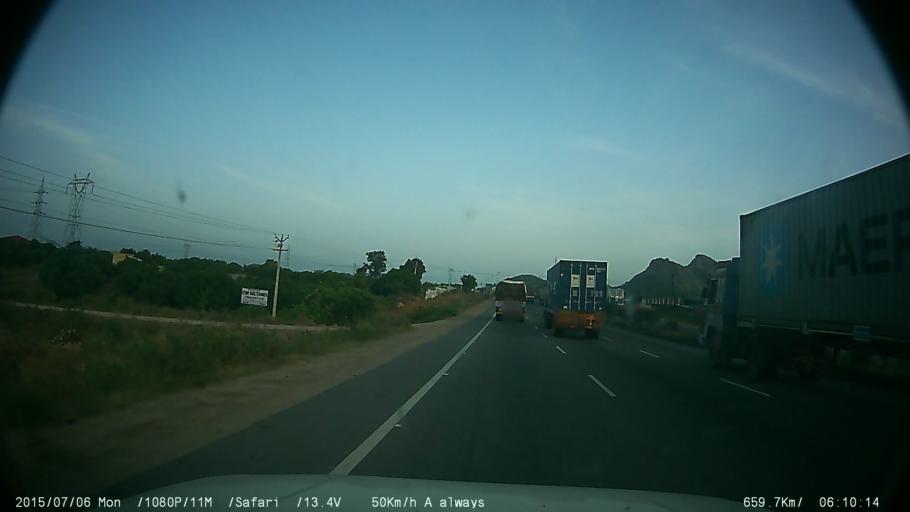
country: IN
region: Tamil Nadu
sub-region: Krishnagiri
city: Kelamangalam
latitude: 12.6505
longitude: 78.0341
